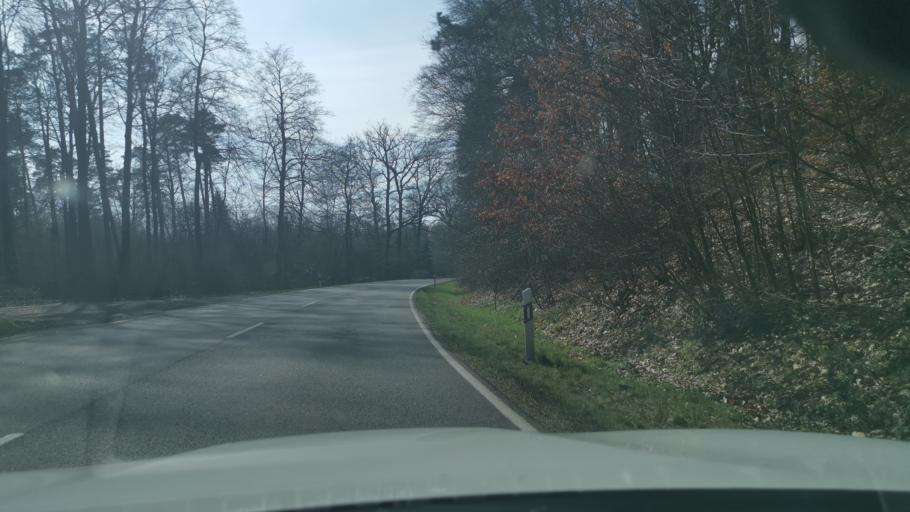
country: DE
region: Saxony
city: Bad Duben
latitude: 51.6636
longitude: 12.5998
